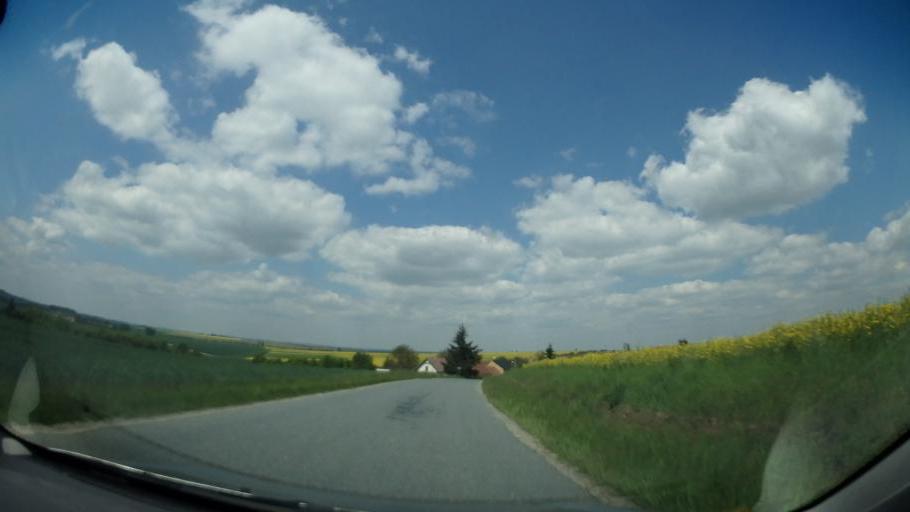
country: CZ
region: Vysocina
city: Hrotovice
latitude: 49.1774
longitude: 16.0833
